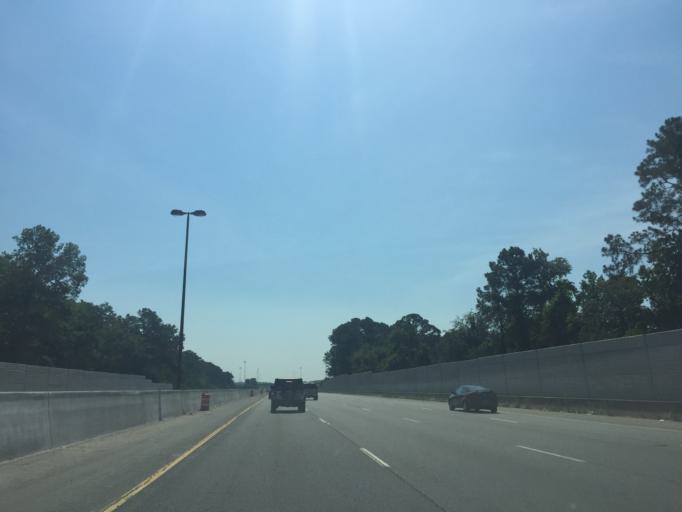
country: US
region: Georgia
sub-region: Chatham County
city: Georgetown
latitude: 31.9848
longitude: -81.2100
